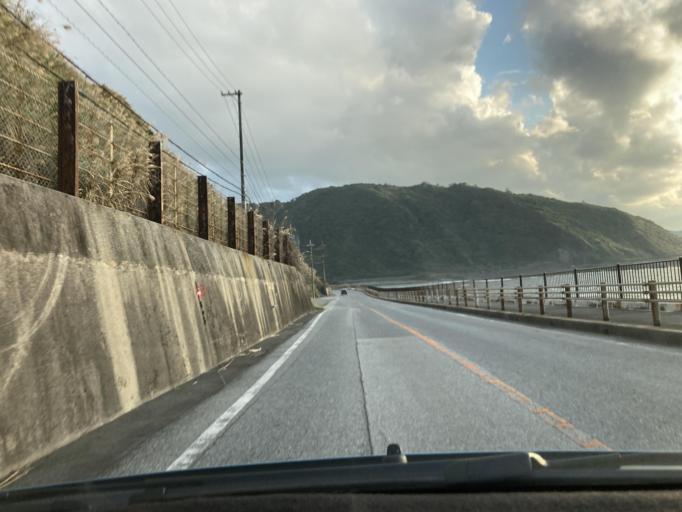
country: JP
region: Okinawa
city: Nago
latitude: 26.8037
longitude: 128.2309
